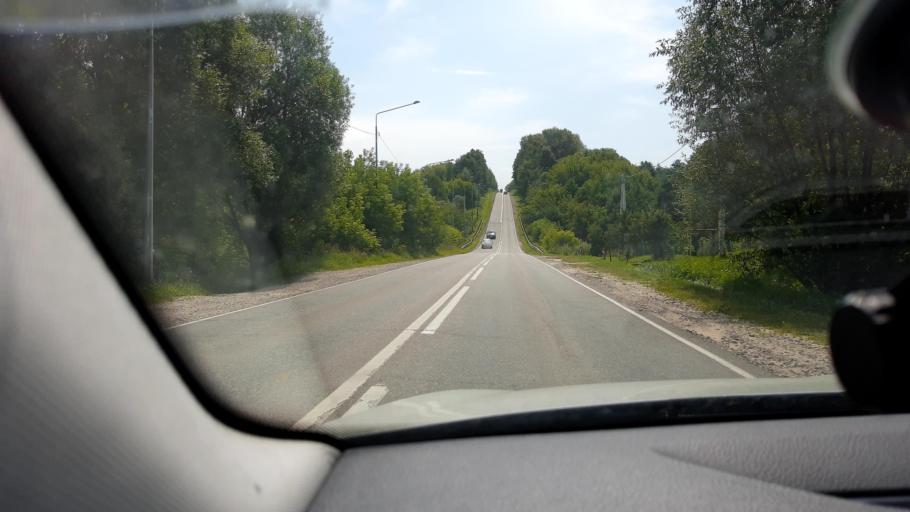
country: RU
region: Tula
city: Zaokskiy
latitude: 54.7938
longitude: 37.4327
